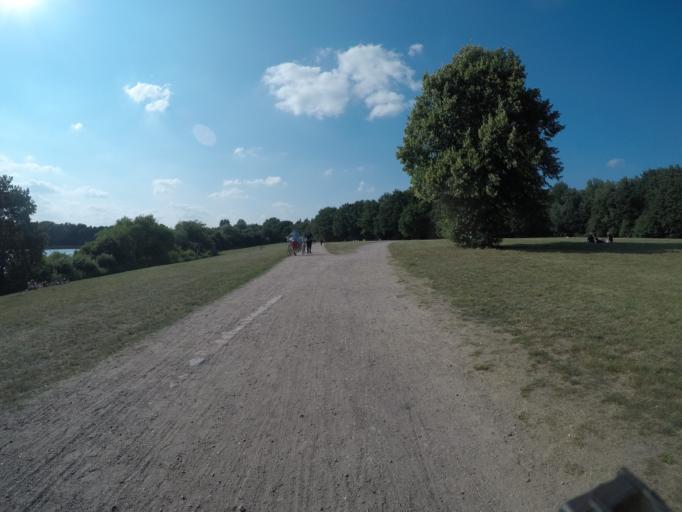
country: DE
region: Schleswig-Holstein
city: Barsbuettel
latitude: 53.5627
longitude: 10.1440
